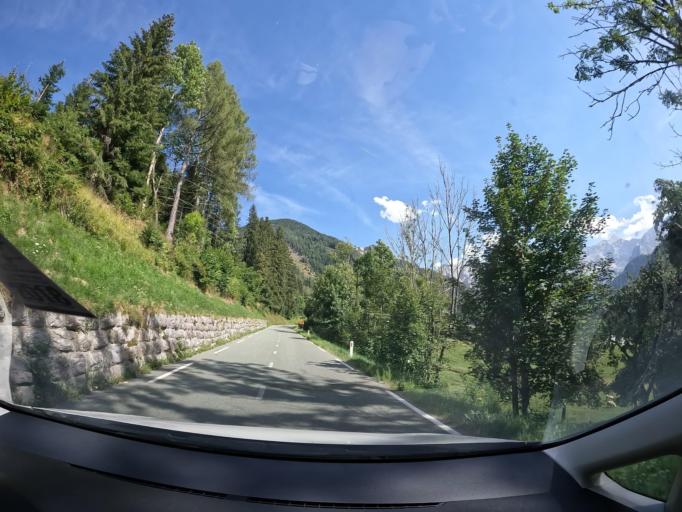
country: AT
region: Carinthia
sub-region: Politischer Bezirk Feldkirchen
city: Glanegg
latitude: 46.7157
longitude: 14.1606
